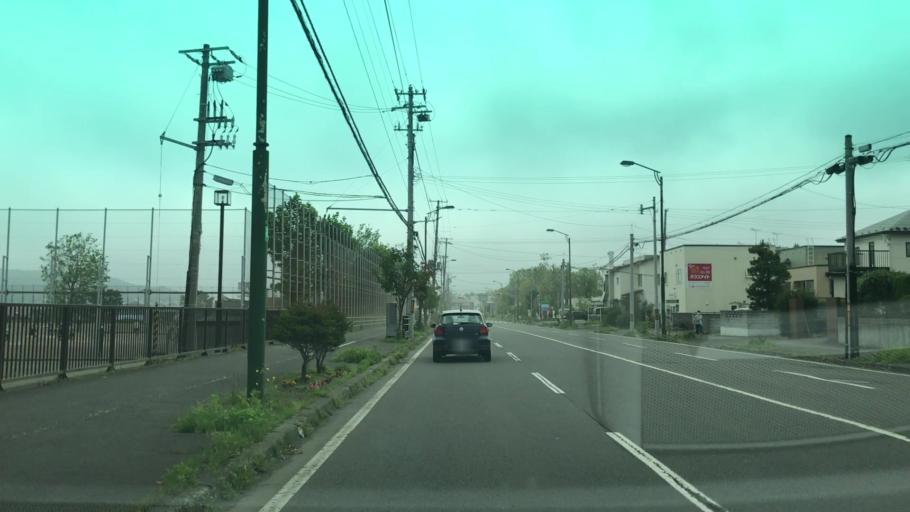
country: JP
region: Hokkaido
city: Muroran
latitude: 42.3693
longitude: 141.0361
